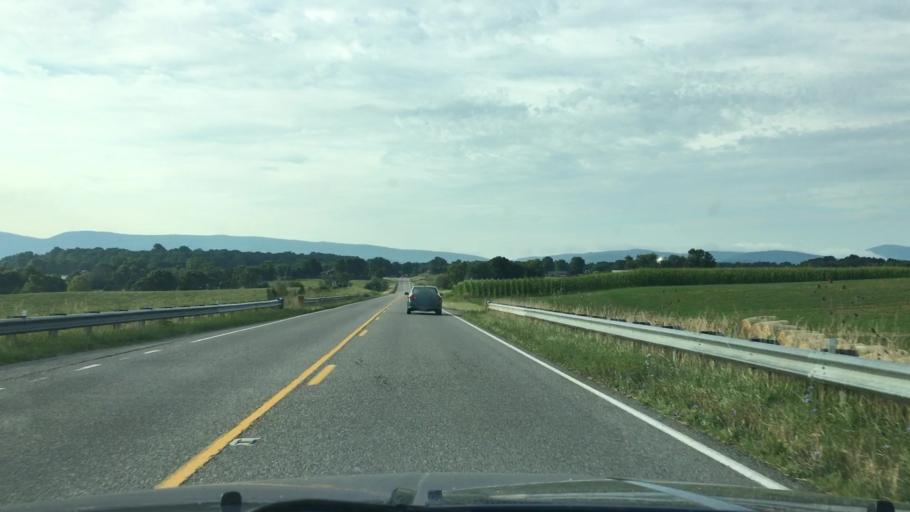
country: US
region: Virginia
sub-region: Augusta County
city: Dooms
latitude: 38.1169
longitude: -78.9091
